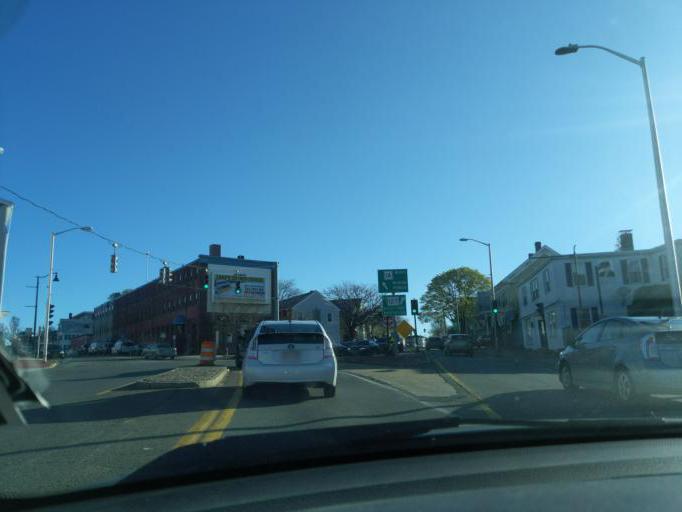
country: US
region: Massachusetts
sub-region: Essex County
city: Beverly
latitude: 42.5417
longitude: -70.8852
